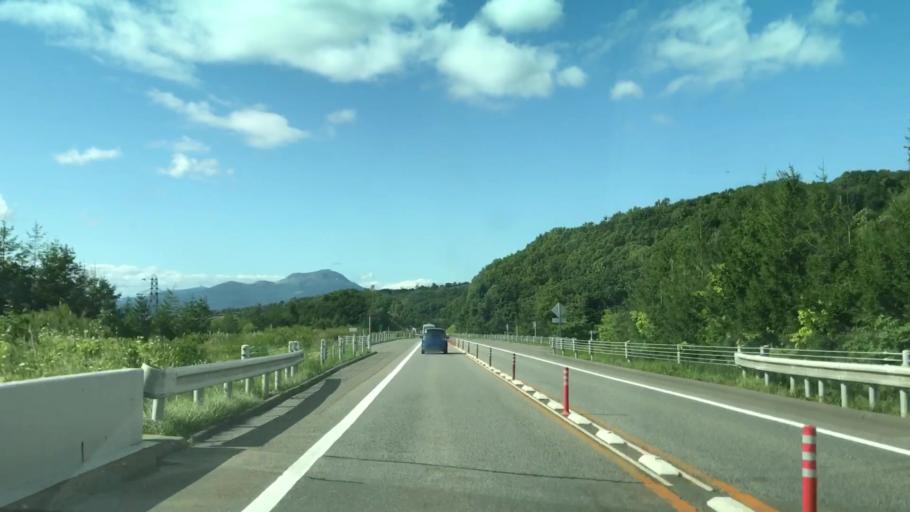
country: JP
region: Hokkaido
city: Date
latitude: 42.4280
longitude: 140.9266
